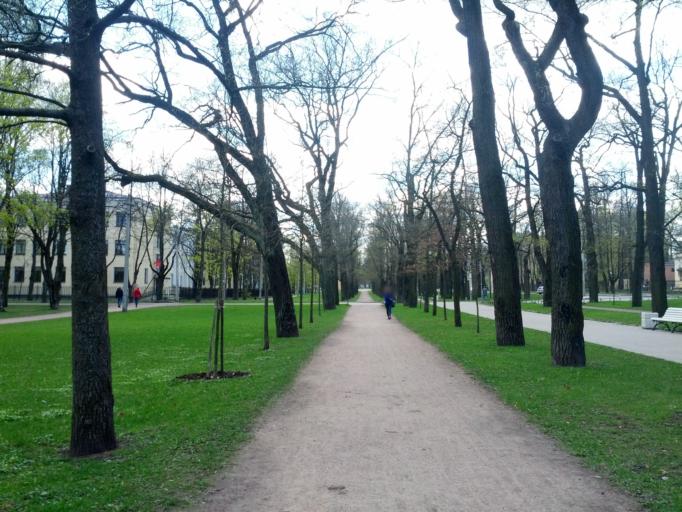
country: RU
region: St.-Petersburg
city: Pushkin
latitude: 59.7184
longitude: 30.4233
